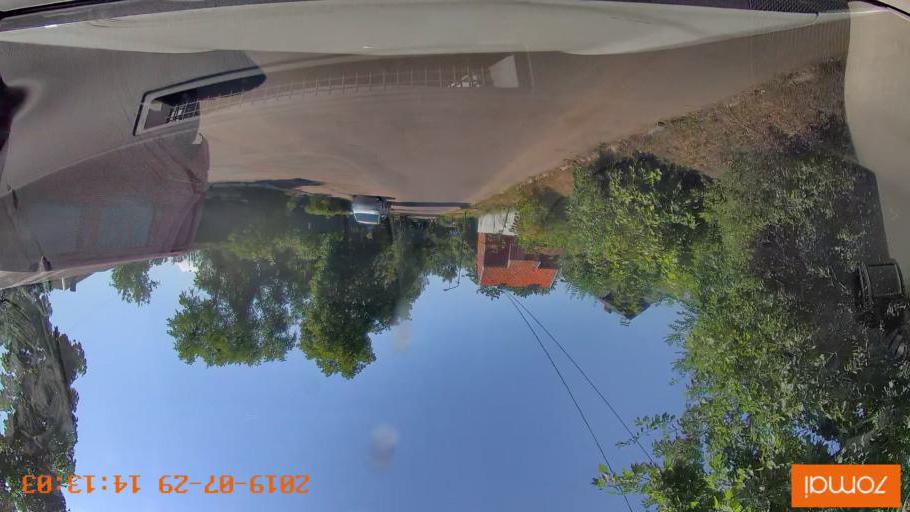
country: RU
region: Kaliningrad
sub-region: Gorod Kaliningrad
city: Baltiysk
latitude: 54.6513
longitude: 19.9029
